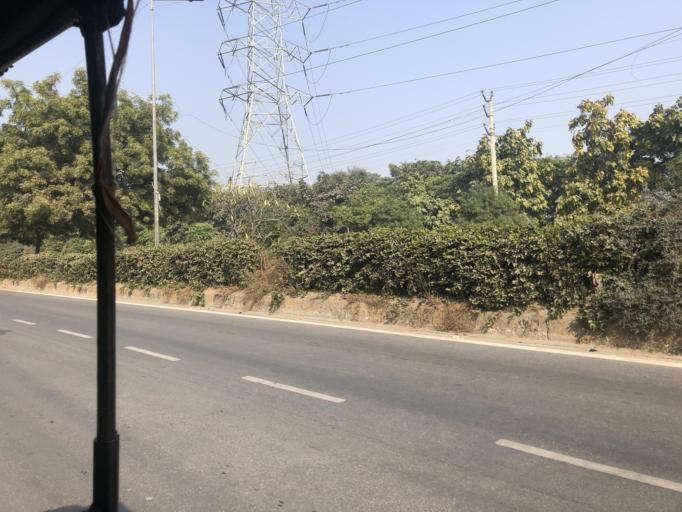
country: IN
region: Haryana
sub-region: Gurgaon
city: Gurgaon
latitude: 28.4439
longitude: 77.0832
